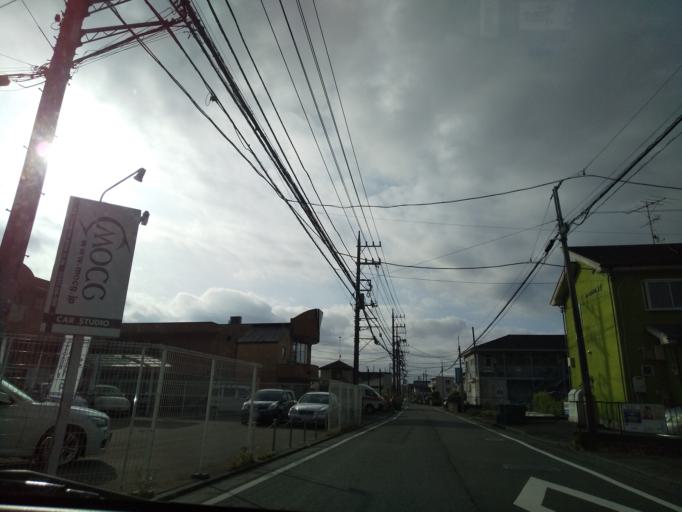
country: JP
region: Tokyo
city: Hachioji
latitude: 35.6847
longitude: 139.3127
